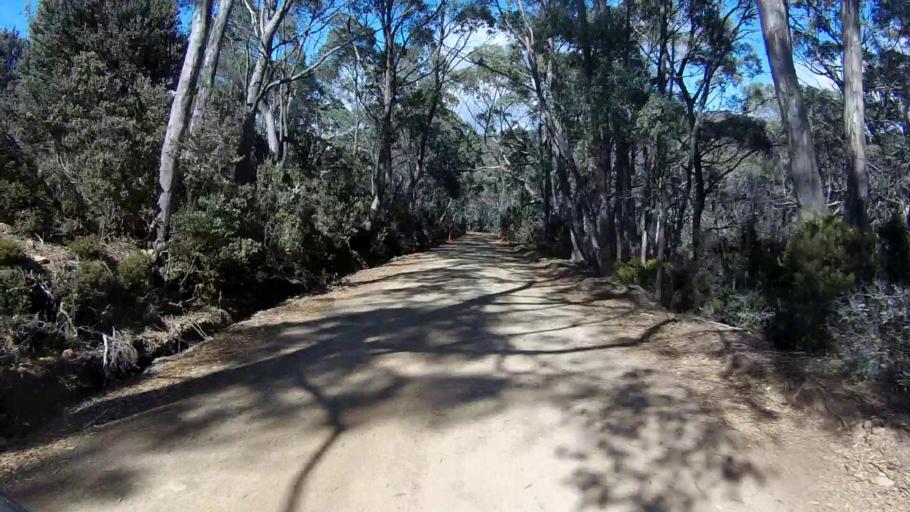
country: AU
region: Tasmania
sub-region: Derwent Valley
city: New Norfolk
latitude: -42.6835
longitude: 146.6070
